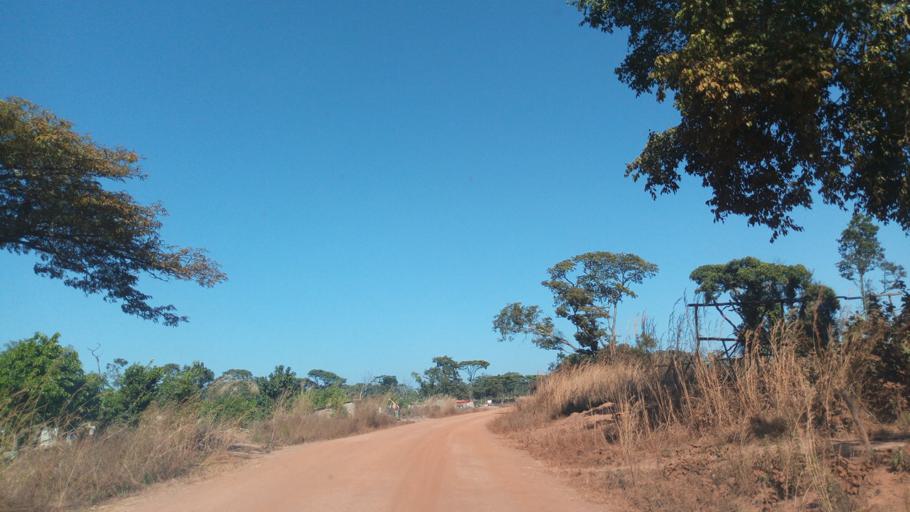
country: ZM
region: Luapula
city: Mwense
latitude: -10.7039
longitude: 28.3761
